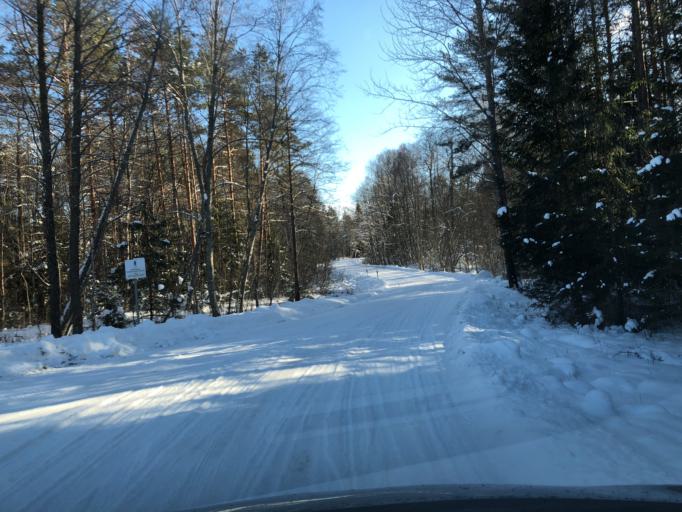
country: EE
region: Jaervamaa
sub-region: Paide linn
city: Paide
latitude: 59.0672
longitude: 25.5101
